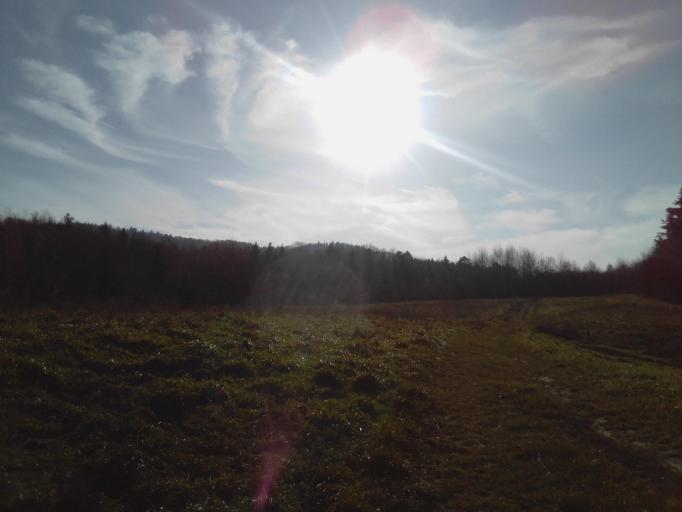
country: PL
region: Subcarpathian Voivodeship
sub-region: Powiat strzyzowski
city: Jawornik
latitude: 49.7985
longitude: 21.8857
